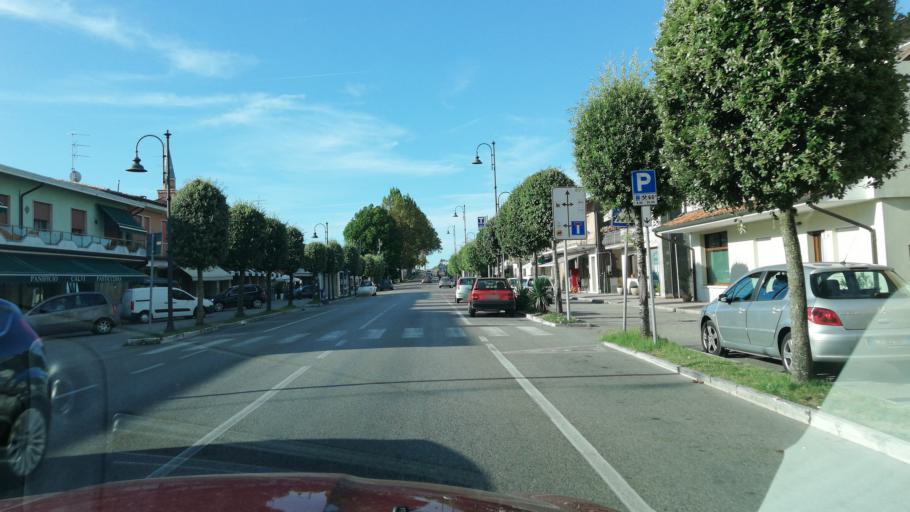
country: IT
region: Veneto
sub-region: Provincia di Venezia
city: La Salute di Livenza
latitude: 45.6591
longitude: 12.8020
